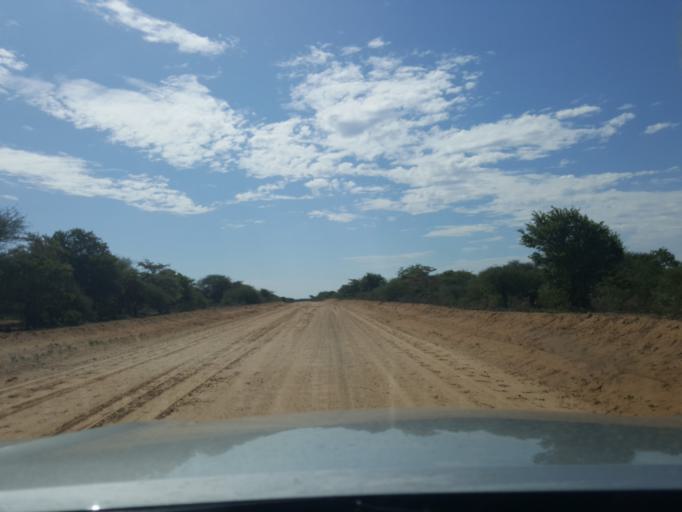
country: BW
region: Kweneng
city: Khudumelapye
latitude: -23.8680
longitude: 24.8937
